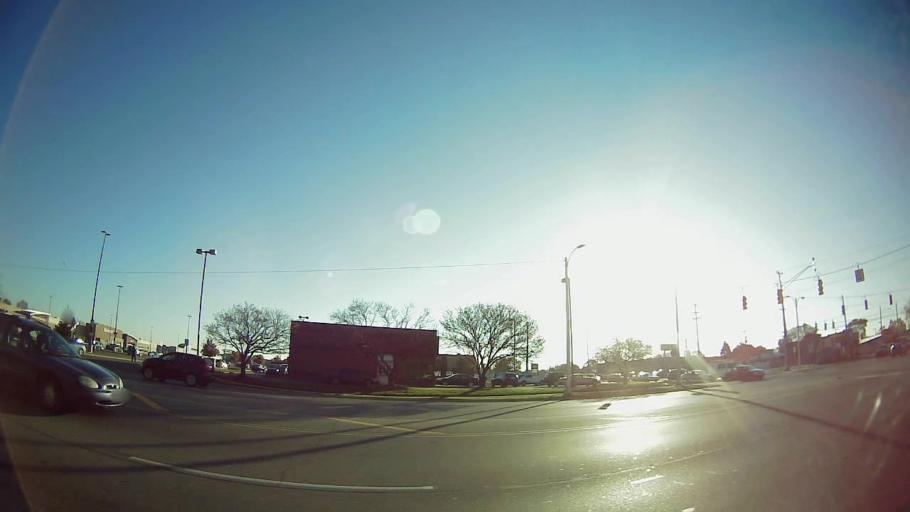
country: US
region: Michigan
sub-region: Macomb County
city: Center Line
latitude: 42.5089
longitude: -83.0286
